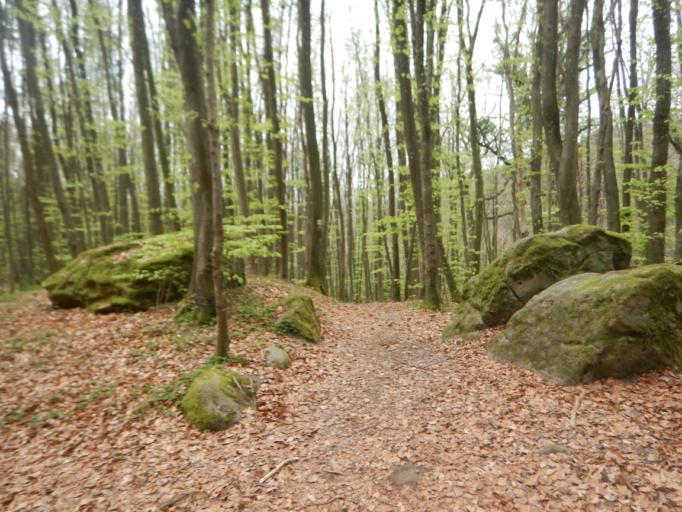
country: LU
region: Grevenmacher
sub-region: Canton d'Echternach
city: Waldbillig
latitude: 49.7962
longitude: 6.3151
